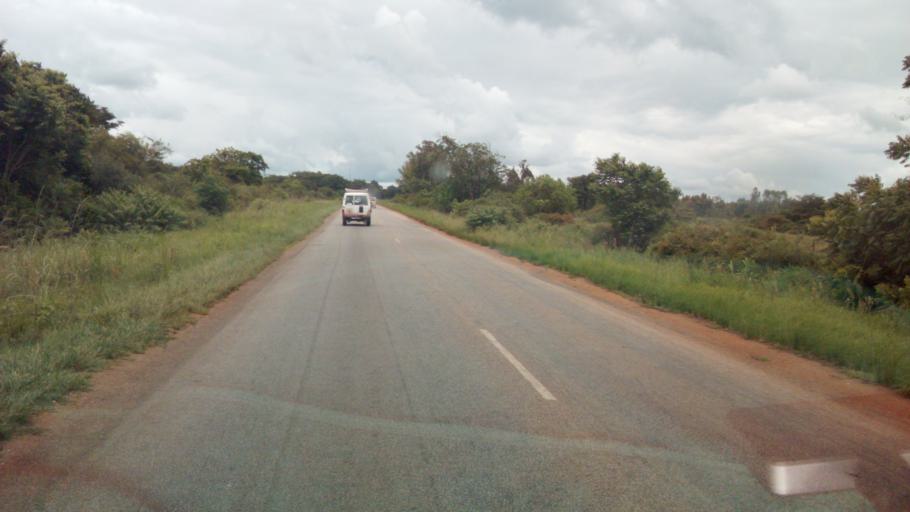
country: ZW
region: Harare
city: Harare
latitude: -17.7155
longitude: 31.0155
